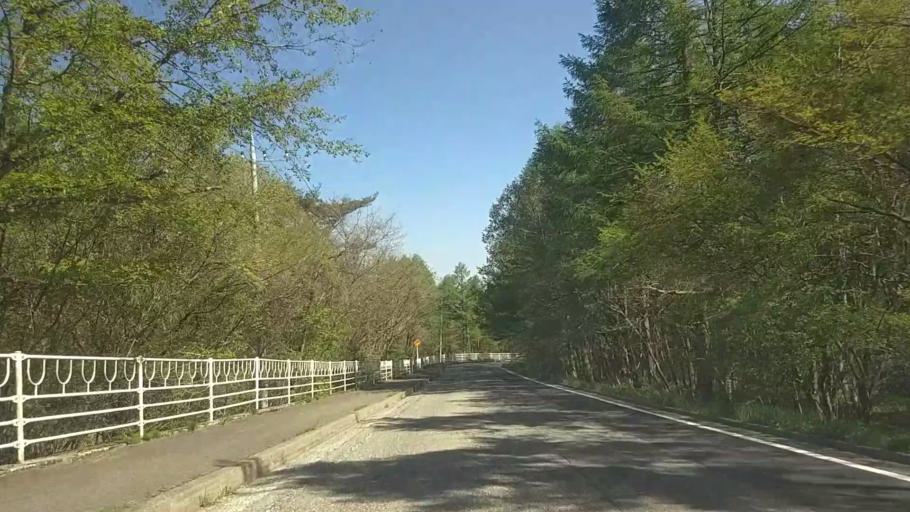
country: JP
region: Yamanashi
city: Nirasaki
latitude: 35.9306
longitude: 138.4186
